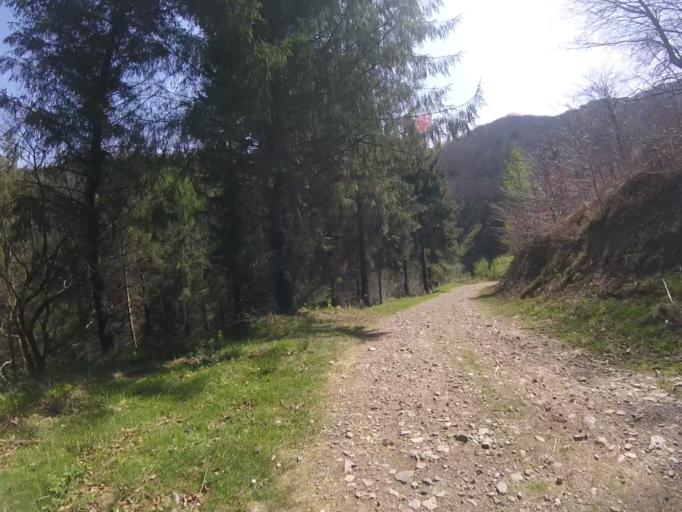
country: ES
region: Basque Country
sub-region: Provincia de Guipuzcoa
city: Irun
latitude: 43.2535
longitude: -1.8068
